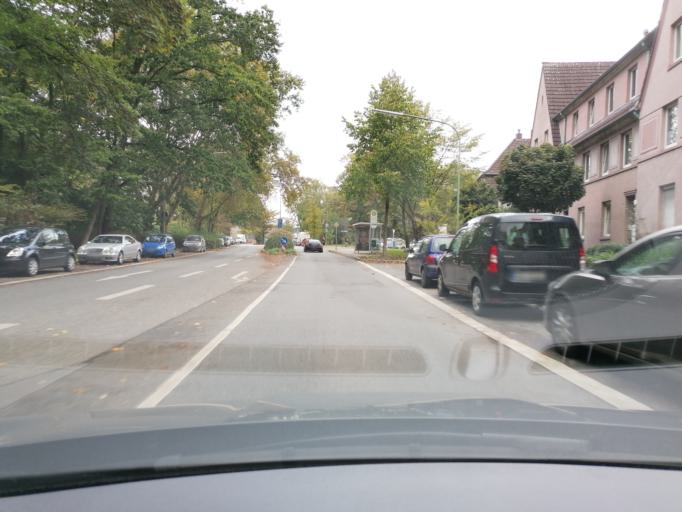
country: DE
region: North Rhine-Westphalia
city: Bochum-Hordel
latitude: 51.5334
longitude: 7.1550
